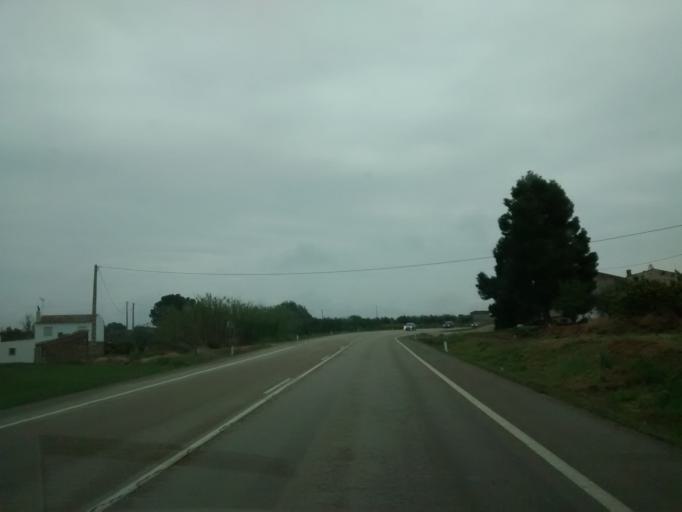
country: ES
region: Aragon
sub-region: Provincia de Zaragoza
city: Caspe
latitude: 41.2226
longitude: -0.0219
